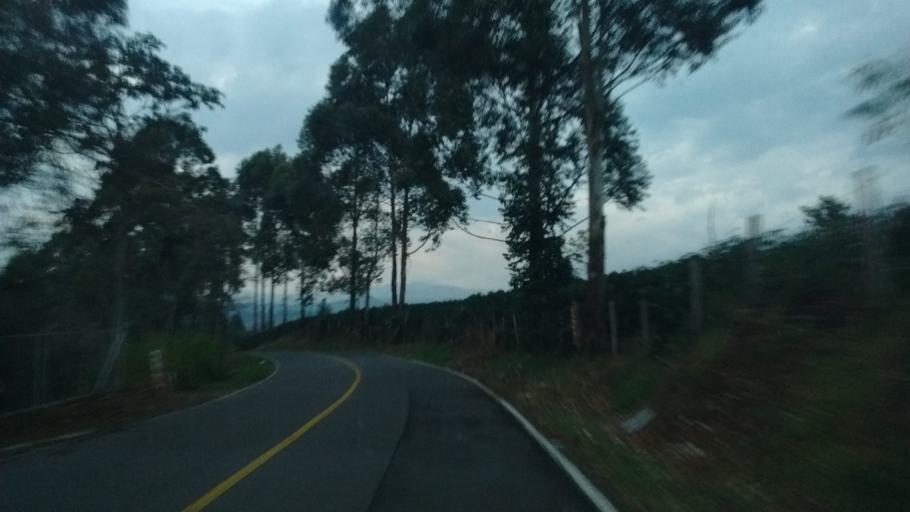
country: CO
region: Cauca
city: Popayan
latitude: 2.3674
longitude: -76.6902
